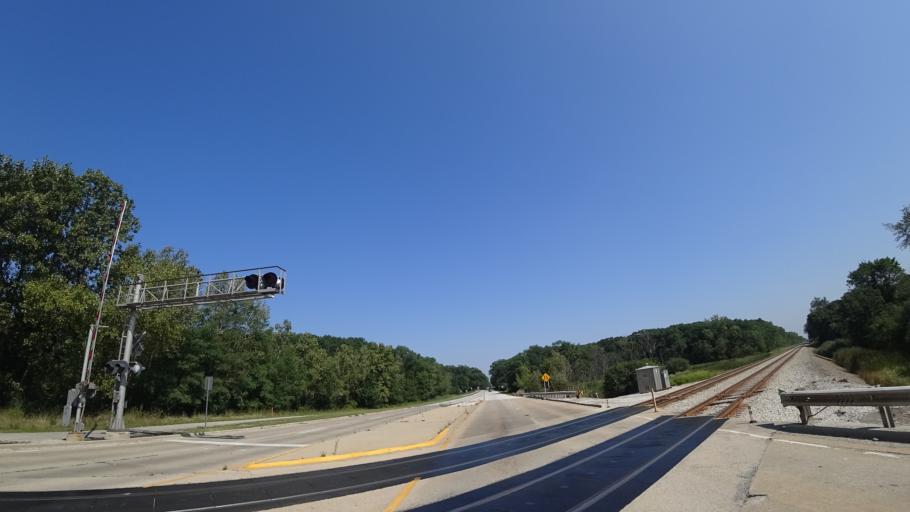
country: US
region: Illinois
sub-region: Cook County
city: Oak Forest
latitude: 41.5902
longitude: -87.7555
